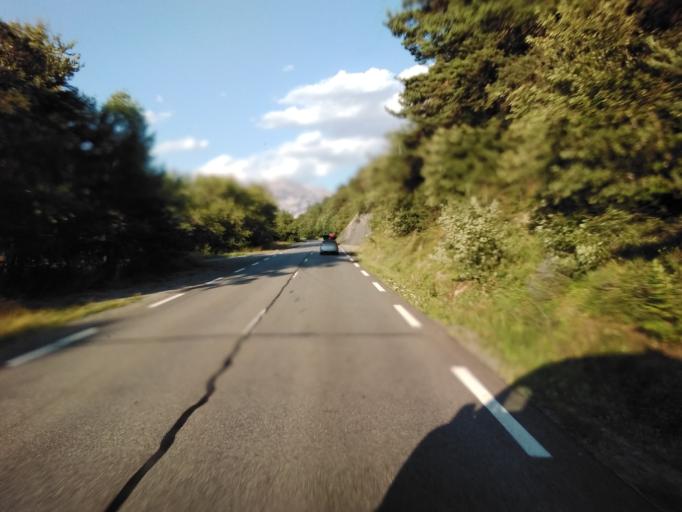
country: FR
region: Provence-Alpes-Cote d'Azur
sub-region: Departement des Hautes-Alpes
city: Chorges
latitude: 44.4556
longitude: 6.3045
